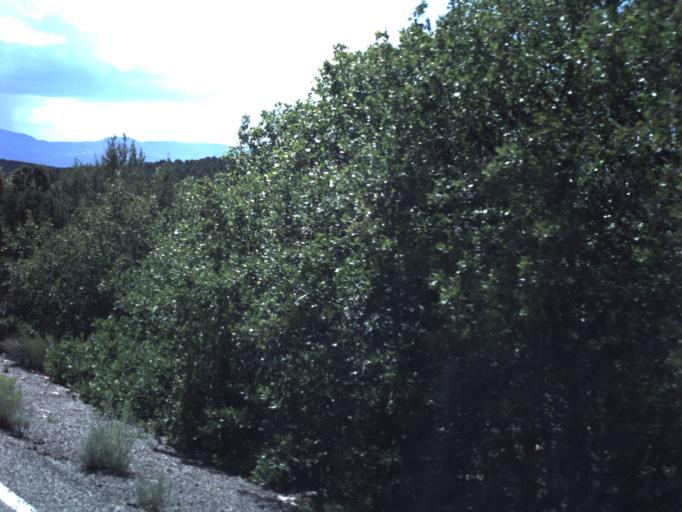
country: US
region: Utah
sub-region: Piute County
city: Junction
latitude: 38.2618
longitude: -112.2958
